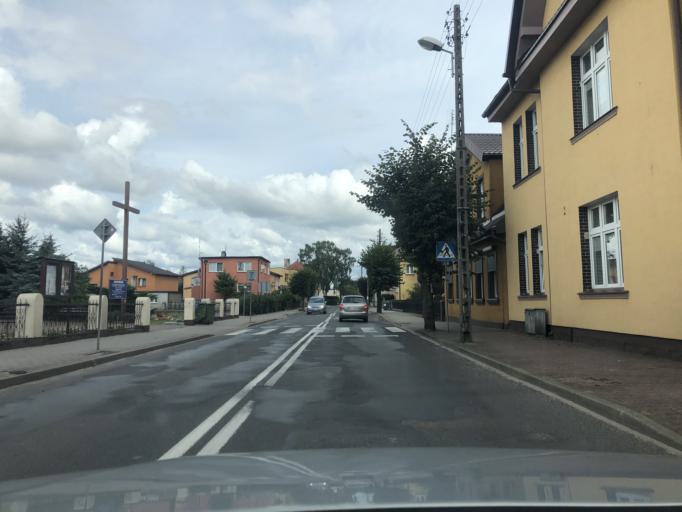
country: PL
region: Greater Poland Voivodeship
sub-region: Powiat czarnkowsko-trzcianecki
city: Krzyz Wielkopolski
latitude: 52.8825
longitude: 16.0164
